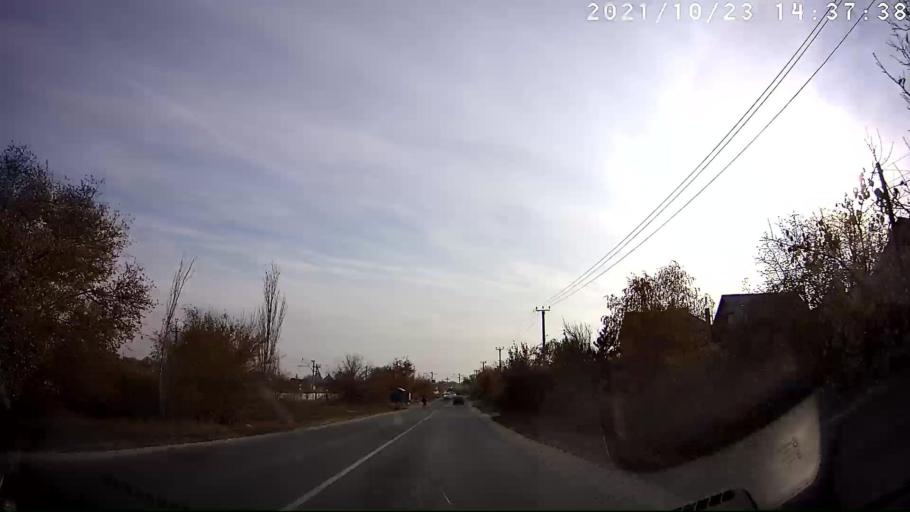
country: RU
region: Volgograd
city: Krasnoslobodsk
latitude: 48.4966
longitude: 44.5495
